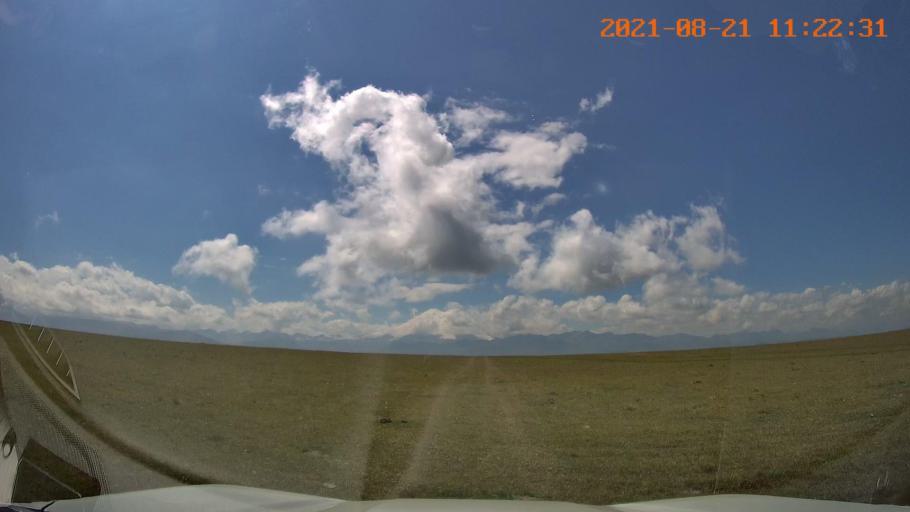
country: RU
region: Stavropol'skiy
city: Kislovodsk
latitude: 43.6151
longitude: 42.5920
